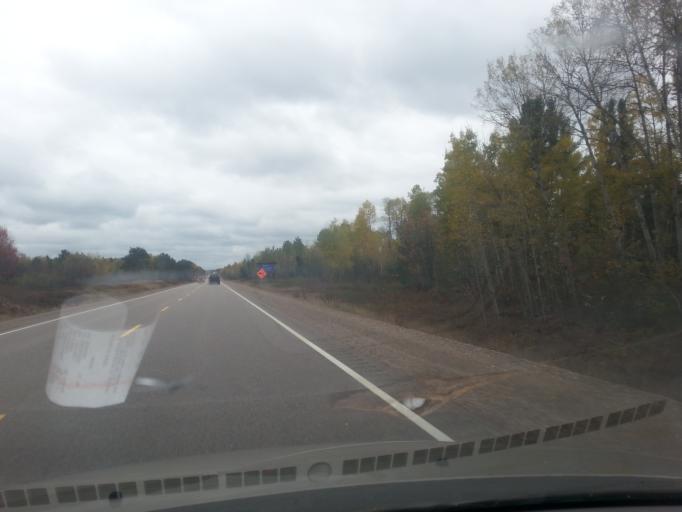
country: CA
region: Ontario
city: Mattawa
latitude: 46.2748
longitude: -78.3709
